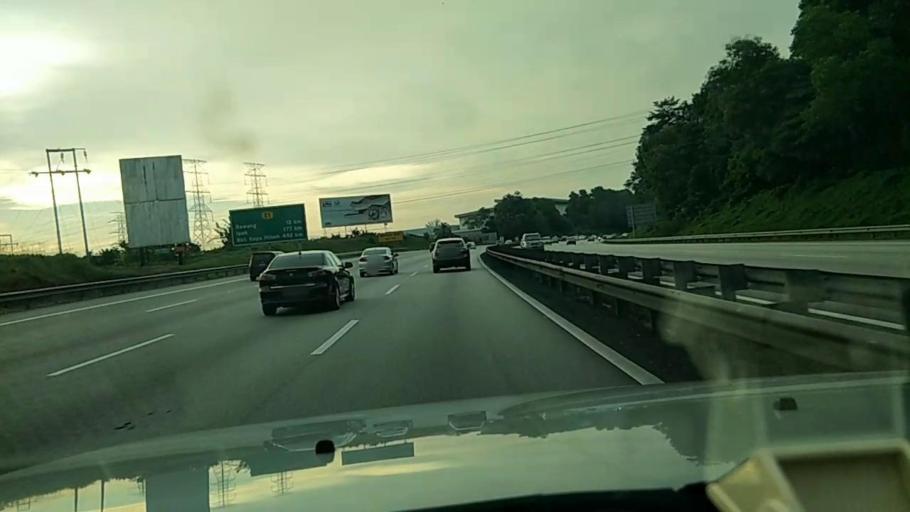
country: MY
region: Selangor
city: Kuang
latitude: 3.2307
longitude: 101.5688
